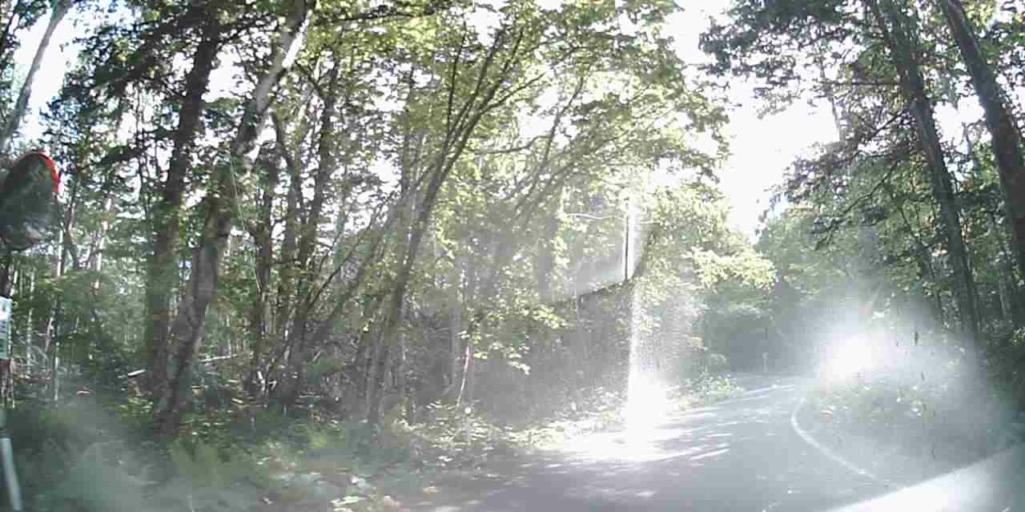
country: JP
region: Hokkaido
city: Shiraoi
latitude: 42.7189
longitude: 141.4102
